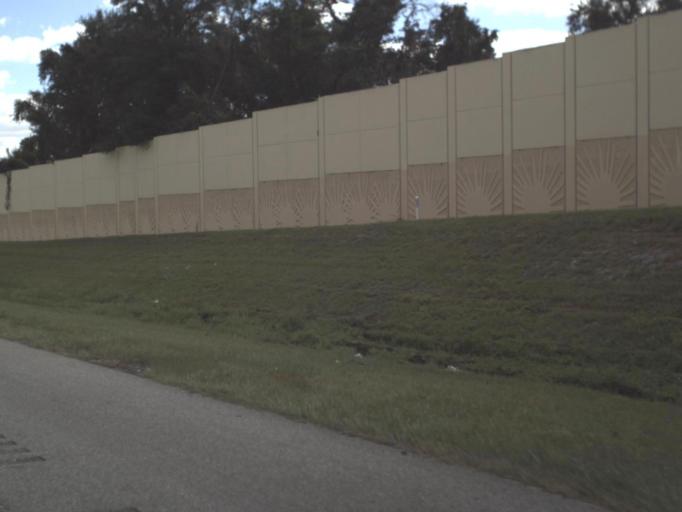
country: US
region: Florida
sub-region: Orange County
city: Orlovista
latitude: 28.4973
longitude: -81.4736
